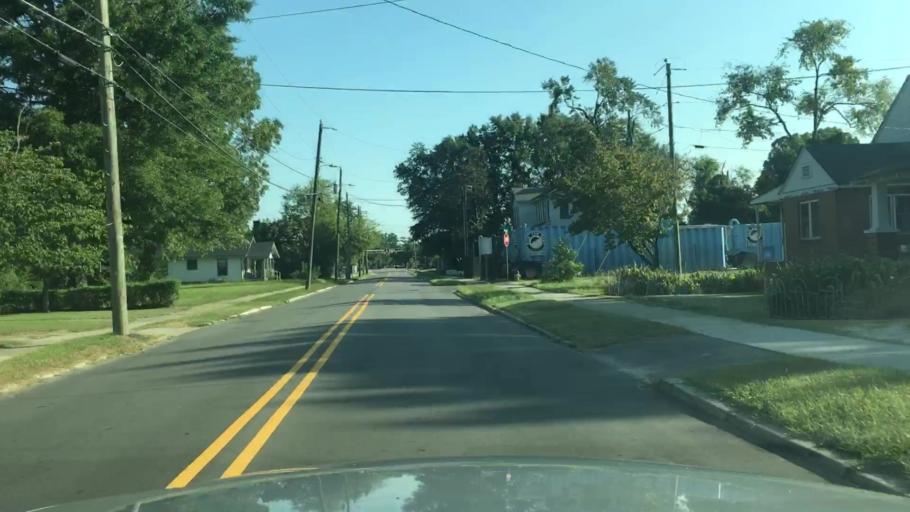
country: US
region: North Carolina
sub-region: Cumberland County
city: Fayetteville
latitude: 35.0467
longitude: -78.8767
